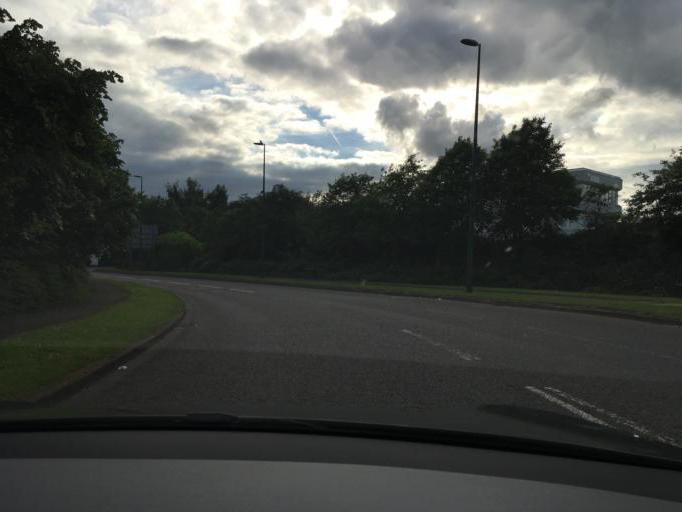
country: GB
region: England
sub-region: Trafford
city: Partington
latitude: 53.4301
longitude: -2.4253
